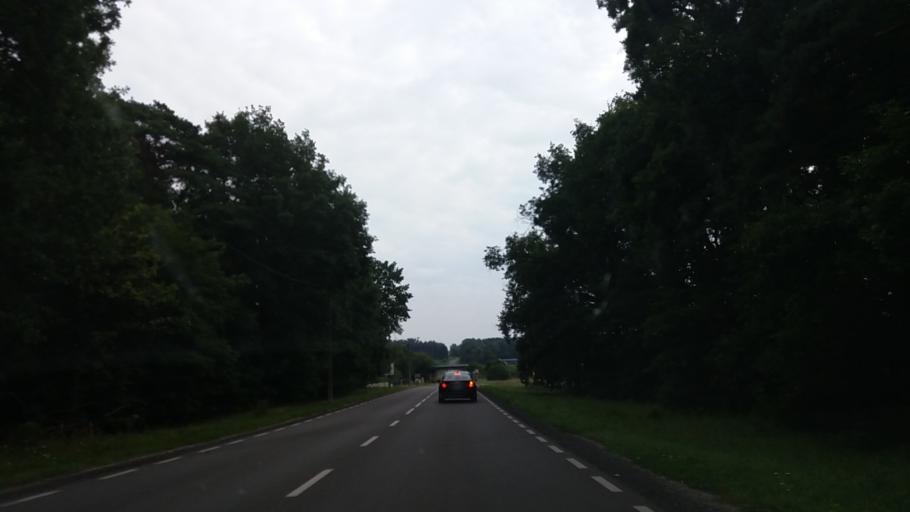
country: PL
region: Lubusz
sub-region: Powiat miedzyrzecki
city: Skwierzyna
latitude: 52.5876
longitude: 15.5123
